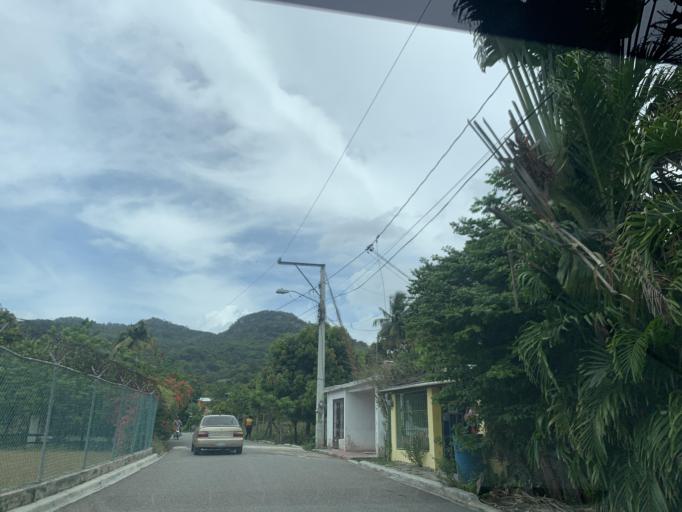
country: DO
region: Puerto Plata
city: Imbert
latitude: 19.8248
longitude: -70.7777
